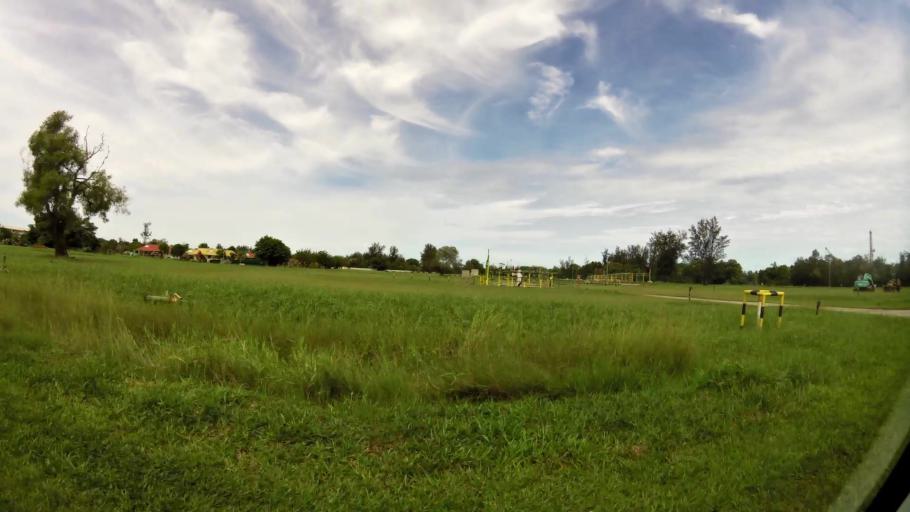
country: BN
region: Belait
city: Seria
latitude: 4.6081
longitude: 114.3120
